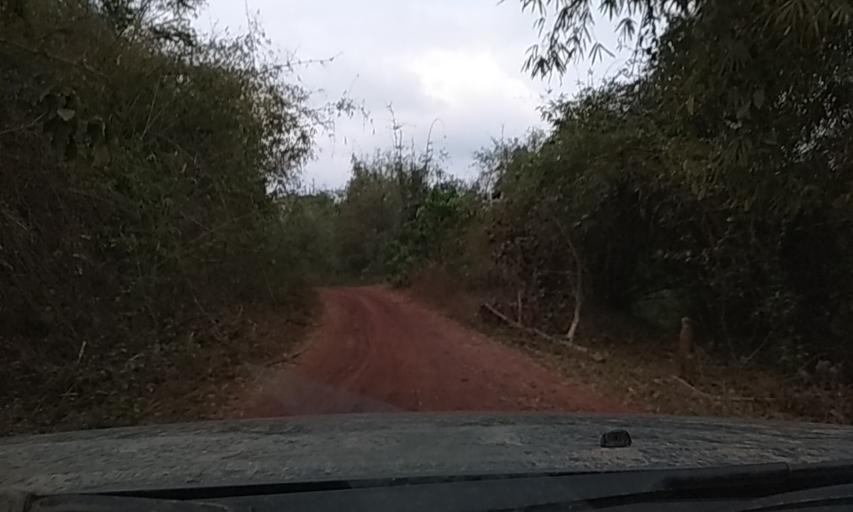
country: TH
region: Nan
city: Mae Charim
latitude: 18.4369
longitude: 101.1855
